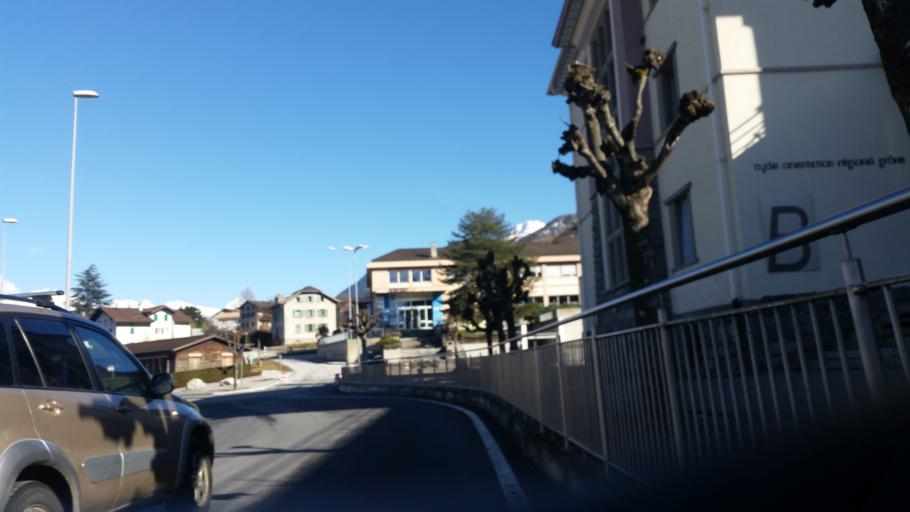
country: CH
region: Valais
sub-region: Sierre District
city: Grone
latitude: 46.2518
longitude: 7.4640
